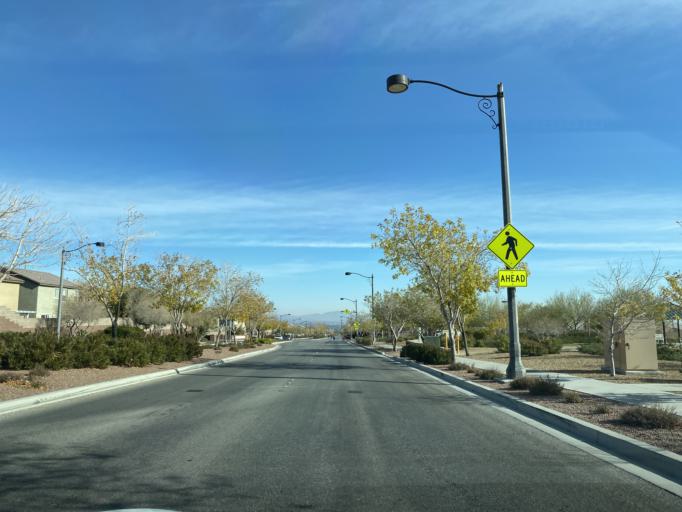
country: US
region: Nevada
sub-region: Clark County
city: Summerlin South
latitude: 36.2882
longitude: -115.3278
